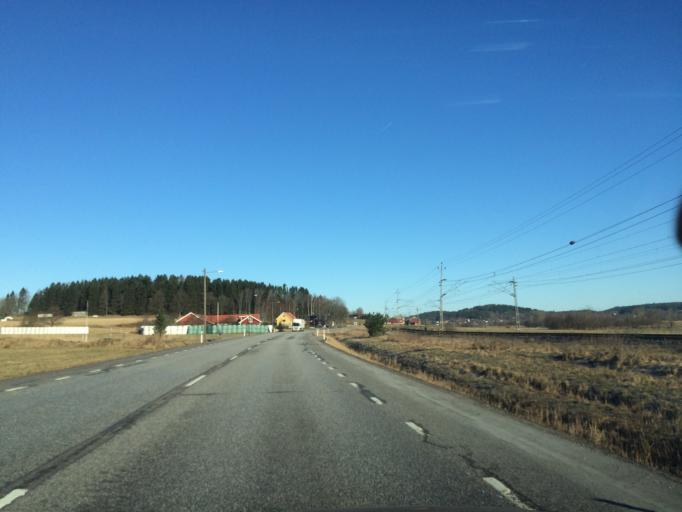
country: SE
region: Vaestra Goetaland
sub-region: Molndal
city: Lindome
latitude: 57.5589
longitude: 12.0849
